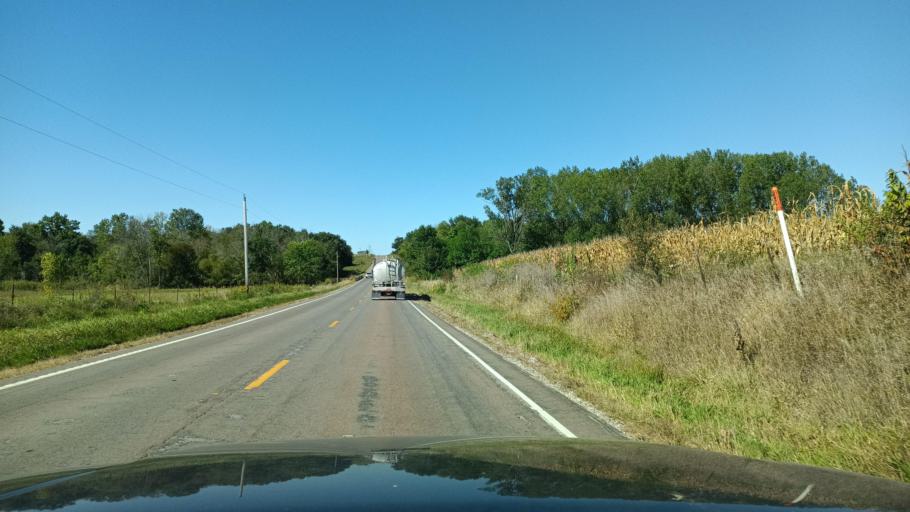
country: US
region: Missouri
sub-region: Scotland County
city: Memphis
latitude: 40.4559
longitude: -92.1174
